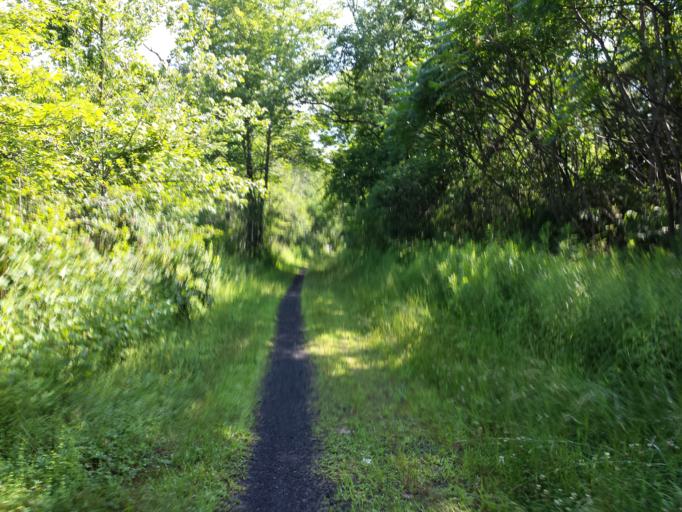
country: US
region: Vermont
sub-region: Rutland County
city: Poultney
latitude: 43.5647
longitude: -73.2218
